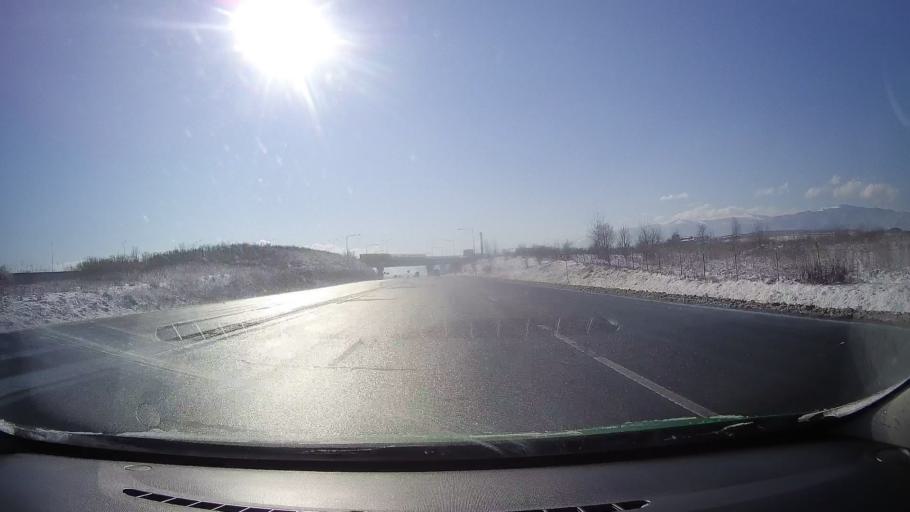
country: RO
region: Sibiu
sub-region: Comuna Selimbar
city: Selimbar
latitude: 45.7506
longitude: 24.2008
